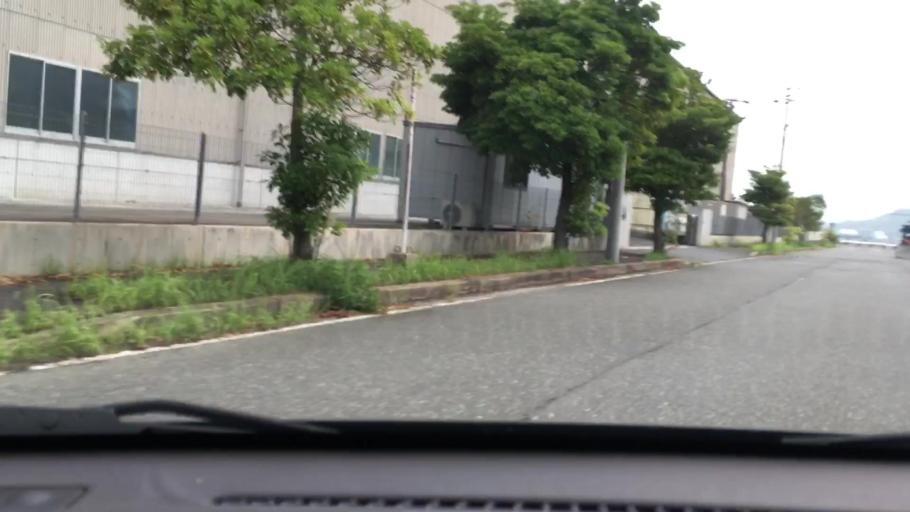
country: JP
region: Yamaguchi
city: Shimonoseki
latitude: 33.8878
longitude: 130.9929
